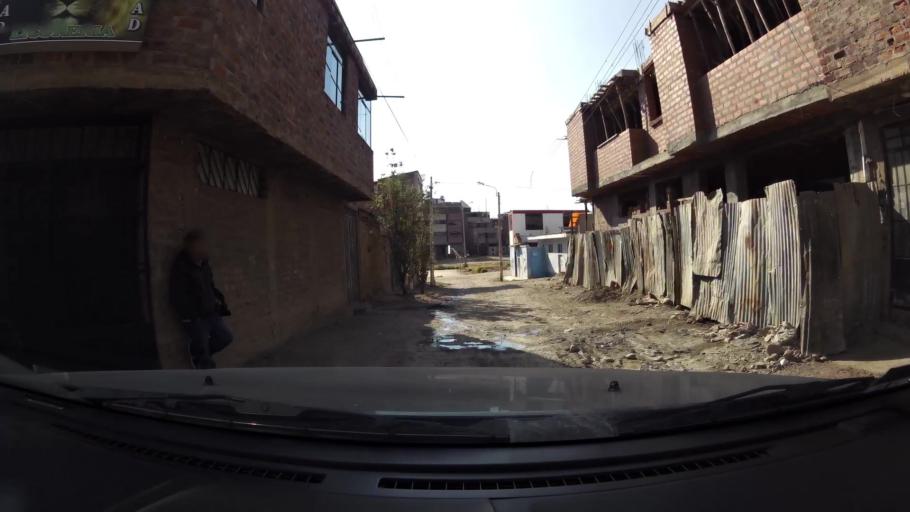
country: PE
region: Junin
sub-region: Provincia de Huancayo
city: El Tambo
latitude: -12.0636
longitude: -75.2221
